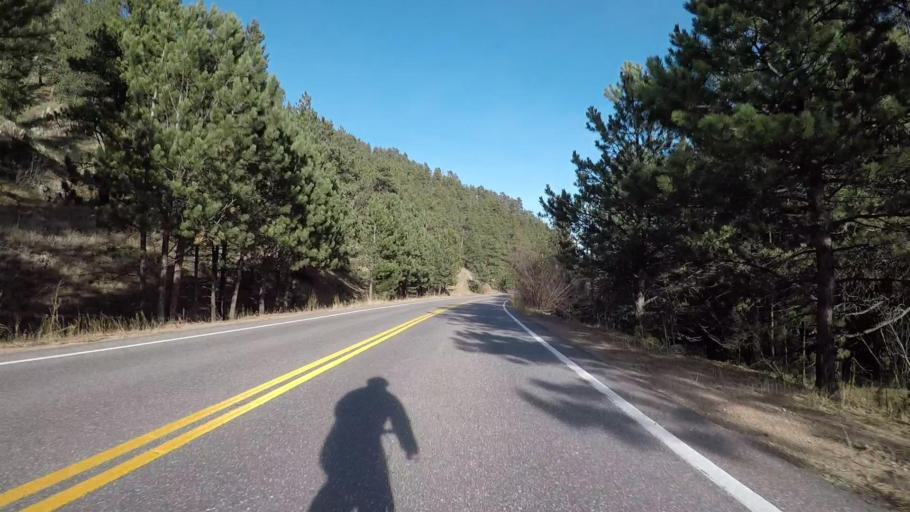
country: US
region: Colorado
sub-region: Boulder County
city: Nederland
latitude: 40.0679
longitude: -105.4463
